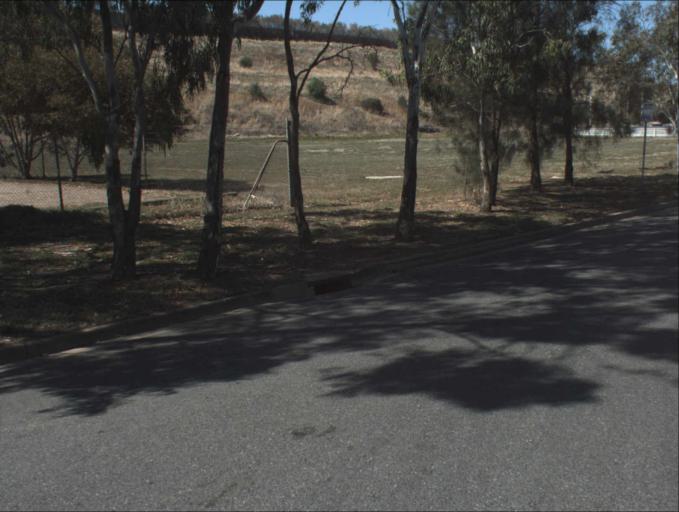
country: AU
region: South Australia
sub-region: Charles Sturt
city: Woodville North
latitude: -34.8372
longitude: 138.5517
